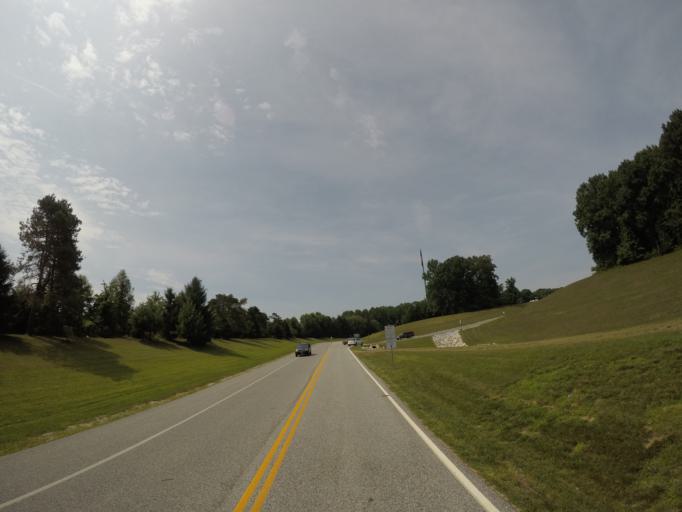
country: US
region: Maryland
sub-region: Howard County
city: Columbia
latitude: 39.3060
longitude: -76.9007
